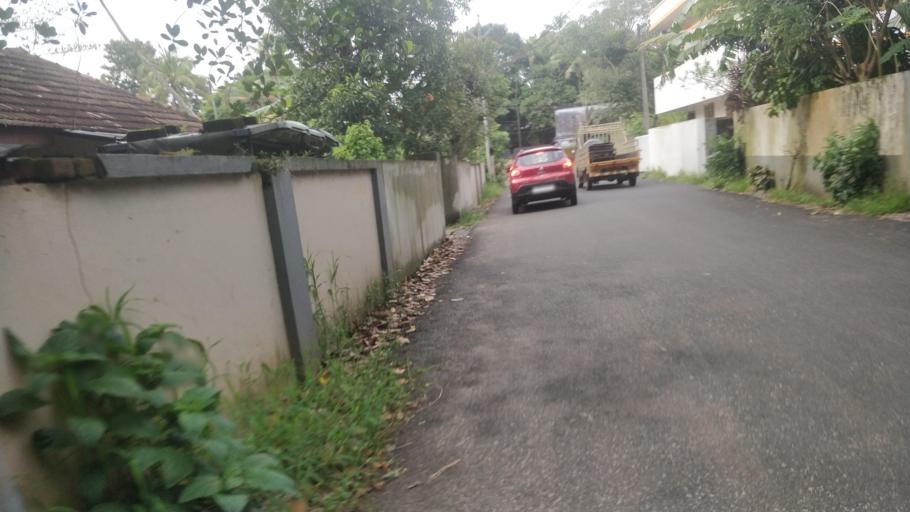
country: IN
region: Kerala
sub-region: Alappuzha
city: Shertallai
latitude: 9.6836
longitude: 76.3528
